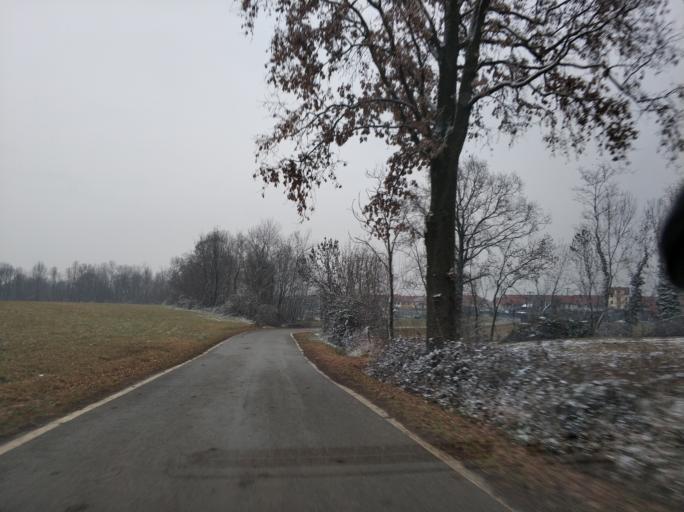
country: IT
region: Piedmont
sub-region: Provincia di Torino
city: San Francesco al Campo
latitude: 45.2311
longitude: 7.6606
